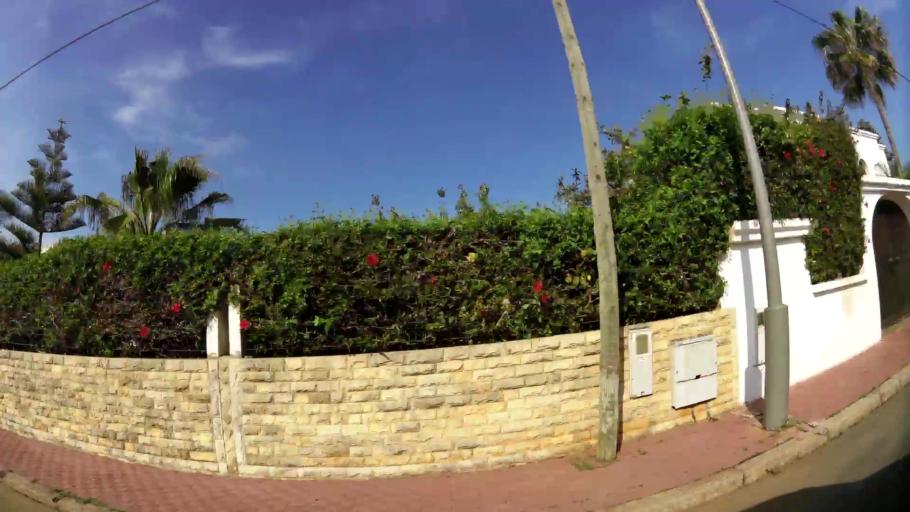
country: MA
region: Rabat-Sale-Zemmour-Zaer
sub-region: Rabat
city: Rabat
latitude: 33.9389
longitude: -6.8064
